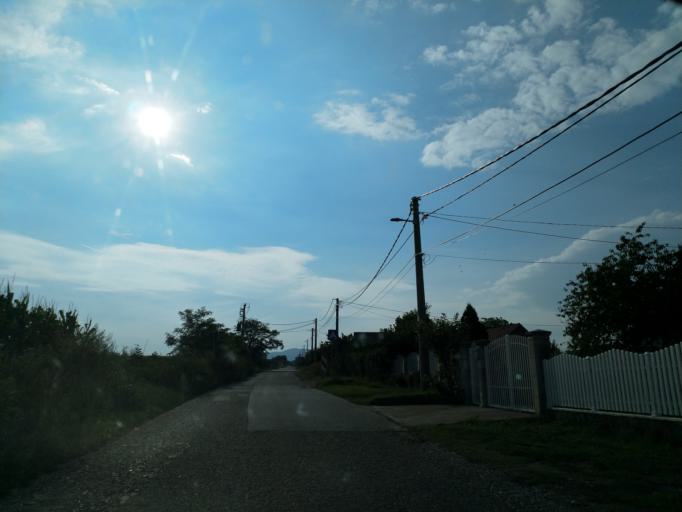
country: RS
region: Central Serbia
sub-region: Pomoravski Okrug
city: Jagodina
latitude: 43.9772
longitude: 21.2380
